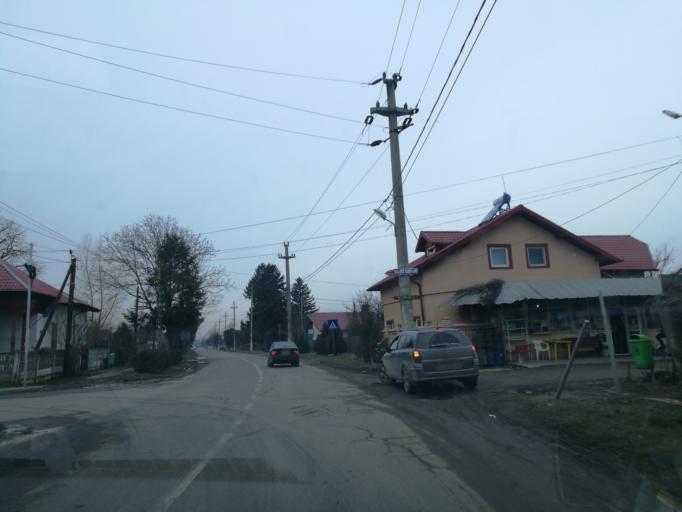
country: RO
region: Ialomita
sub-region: Comuna Fierbinti-Targ
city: Fierbintii de Jos
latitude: 44.6823
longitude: 26.3767
